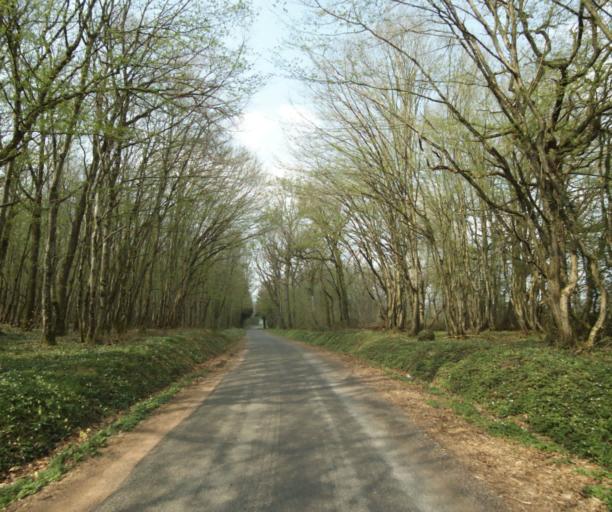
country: FR
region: Bourgogne
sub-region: Departement de Saone-et-Loire
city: Charolles
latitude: 46.4656
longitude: 4.3468
